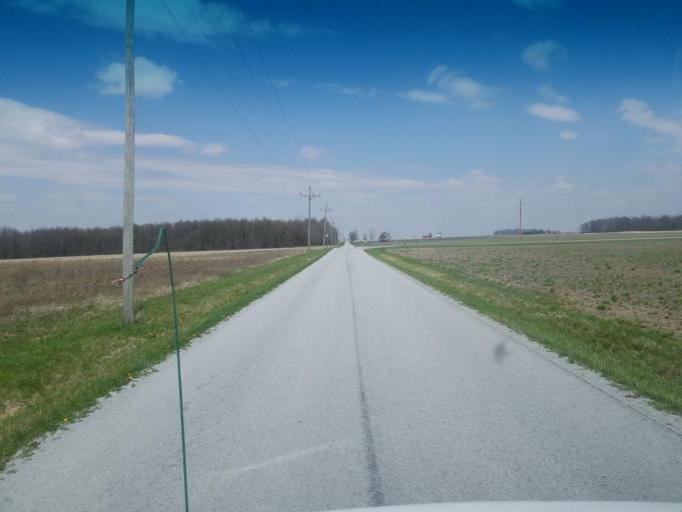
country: US
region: Ohio
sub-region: Hardin County
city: Forest
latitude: 40.7734
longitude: -83.4967
